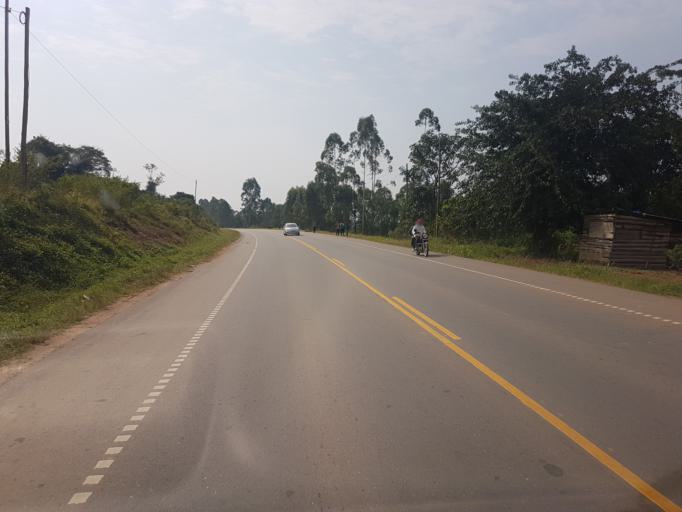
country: UG
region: Western Region
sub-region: Mbarara District
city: Bwizibwera
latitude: -0.6427
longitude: 30.5603
